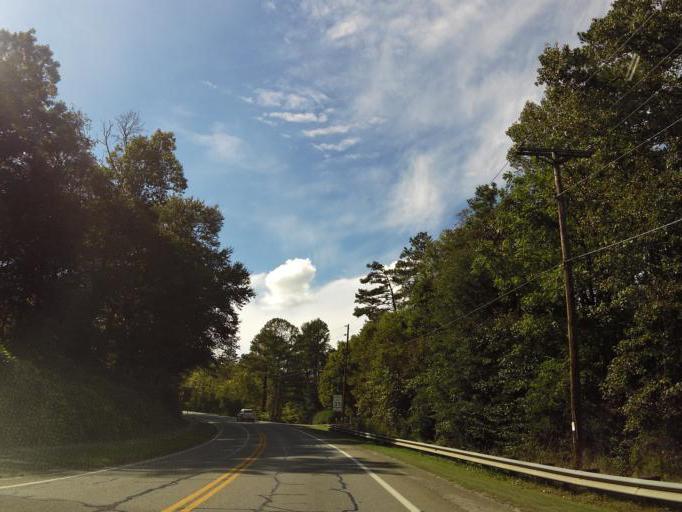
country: US
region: Georgia
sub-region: Pickens County
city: Nelson
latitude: 34.4187
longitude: -84.3817
